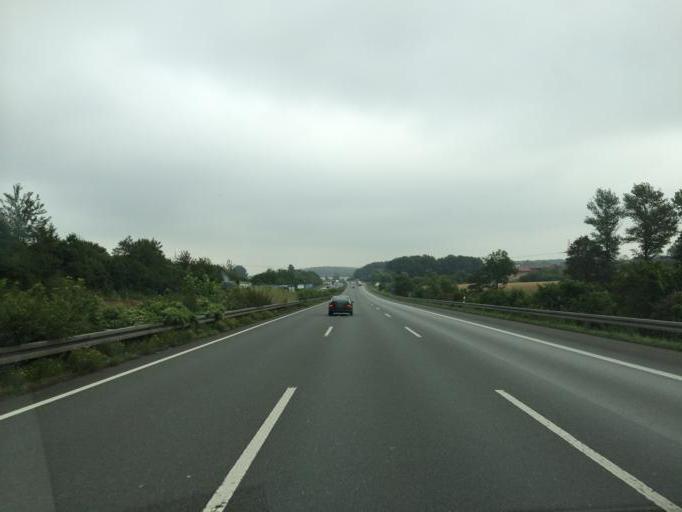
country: DE
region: North Rhine-Westphalia
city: Oelde
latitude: 51.8050
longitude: 8.1218
